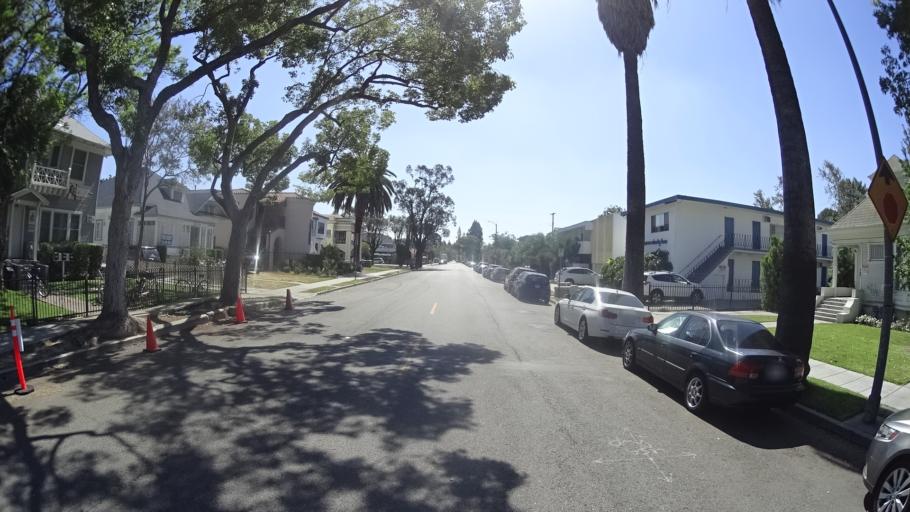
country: US
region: California
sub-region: Los Angeles County
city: Los Angeles
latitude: 34.0274
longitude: -118.2895
